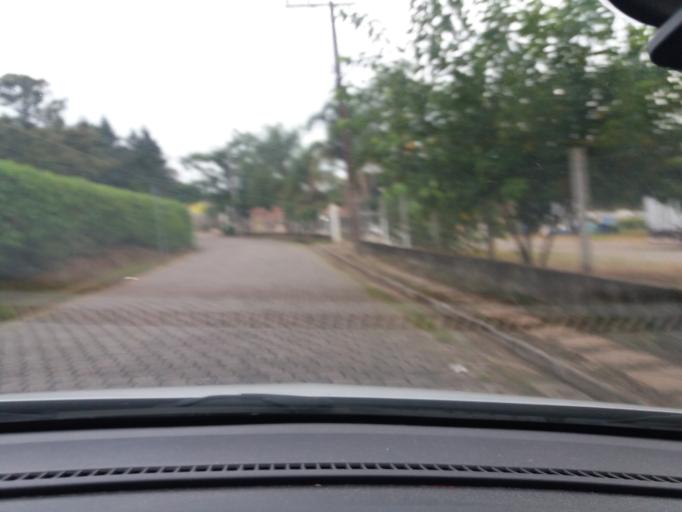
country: BR
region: Sao Paulo
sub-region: Bom Jesus Dos Perdoes
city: Bom Jesus dos Perdoes
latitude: -23.1628
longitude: -46.4515
